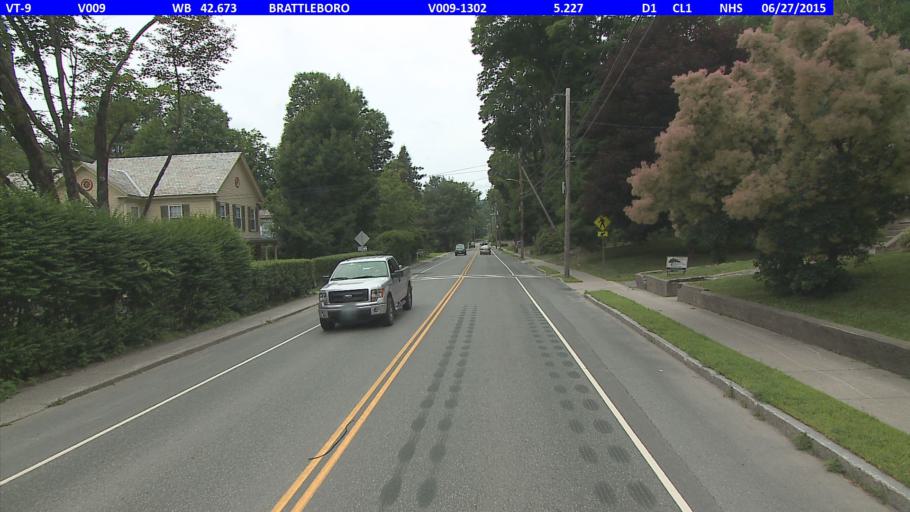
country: US
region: Vermont
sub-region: Windham County
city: West Brattleboro
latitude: 42.8508
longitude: -72.5919
